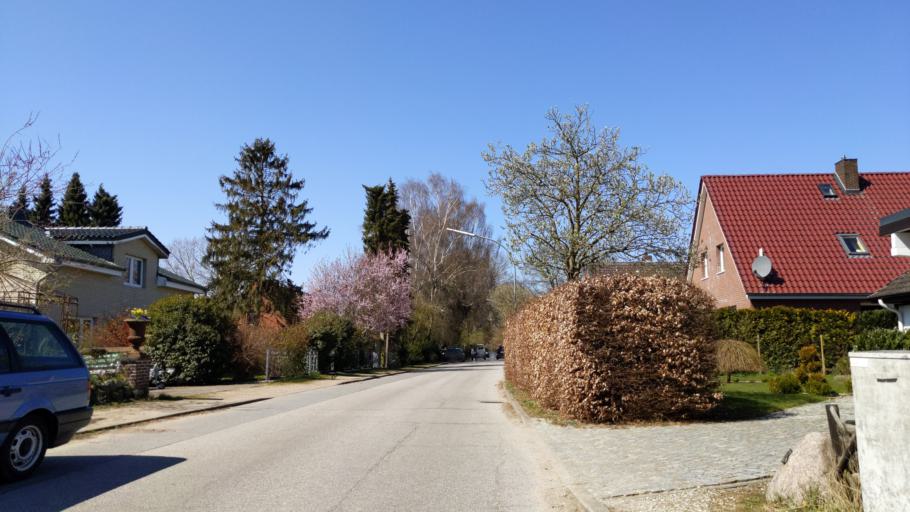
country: DE
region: Schleswig-Holstein
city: Ratekau
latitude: 53.9694
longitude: 10.6989
